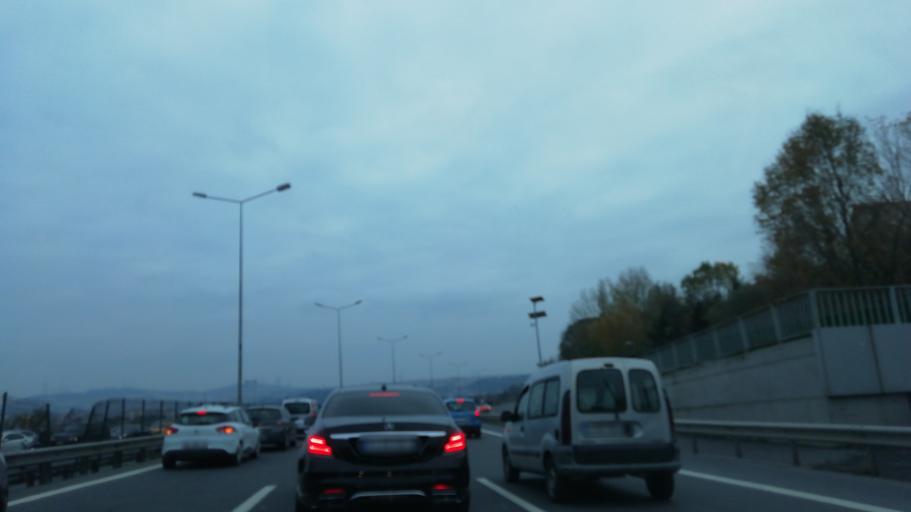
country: TR
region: Istanbul
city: Sisli
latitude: 41.0648
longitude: 29.0147
